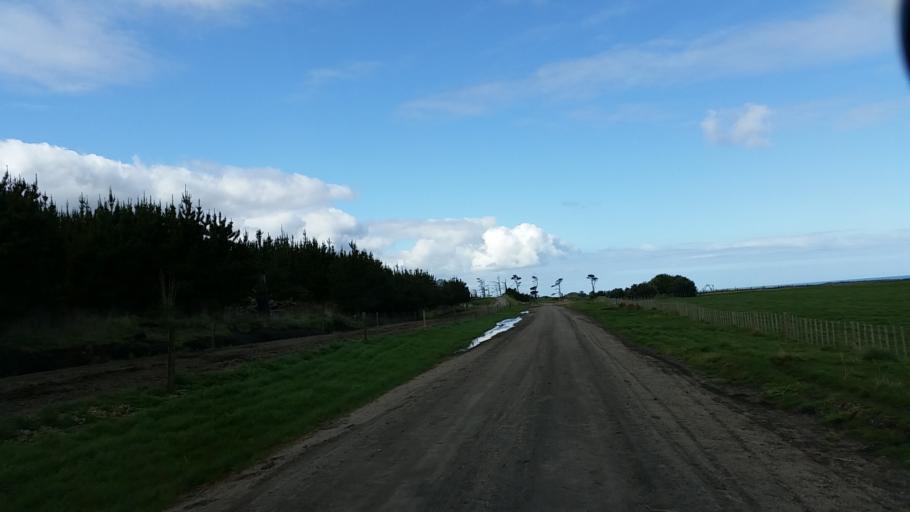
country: NZ
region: Taranaki
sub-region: South Taranaki District
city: Patea
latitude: -39.7975
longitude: 174.5920
